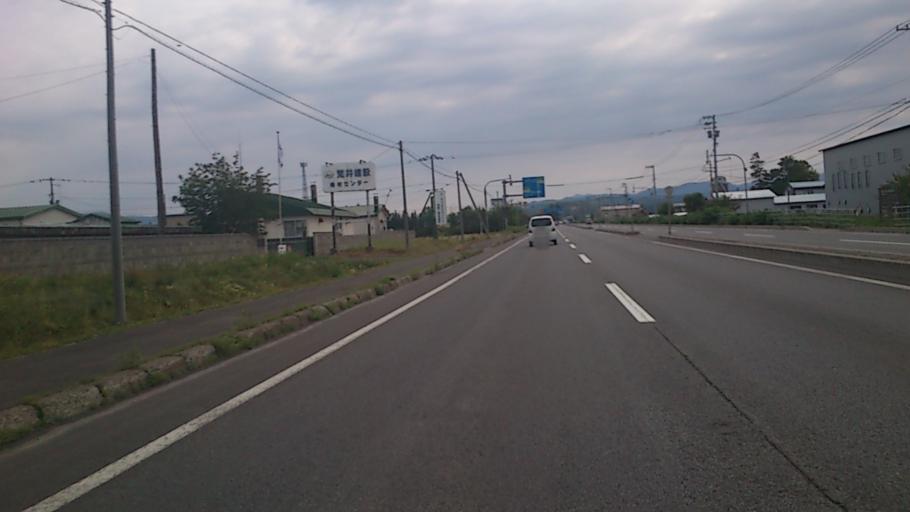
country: JP
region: Hokkaido
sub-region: Asahikawa-shi
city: Asahikawa
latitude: 43.8524
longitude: 142.5009
